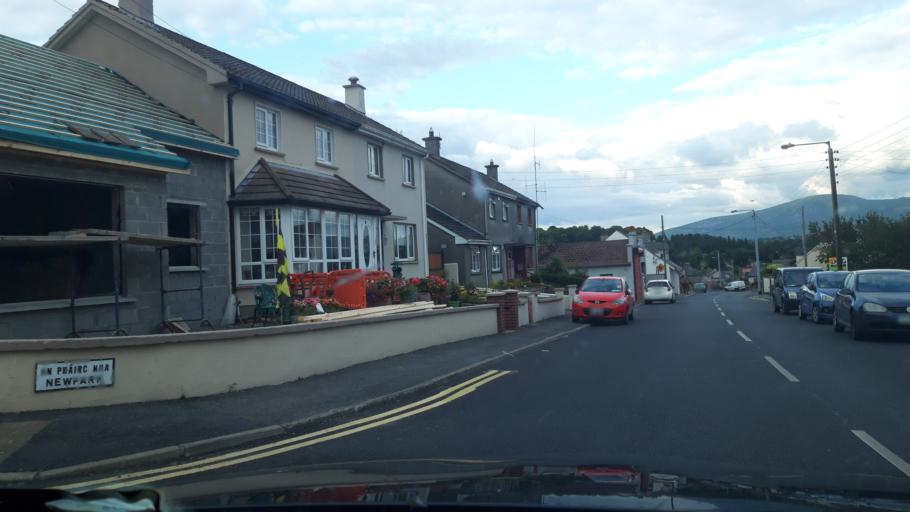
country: IE
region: Leinster
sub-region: Kilkenny
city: Graiguenamanagh
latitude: 52.5406
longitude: -6.9615
